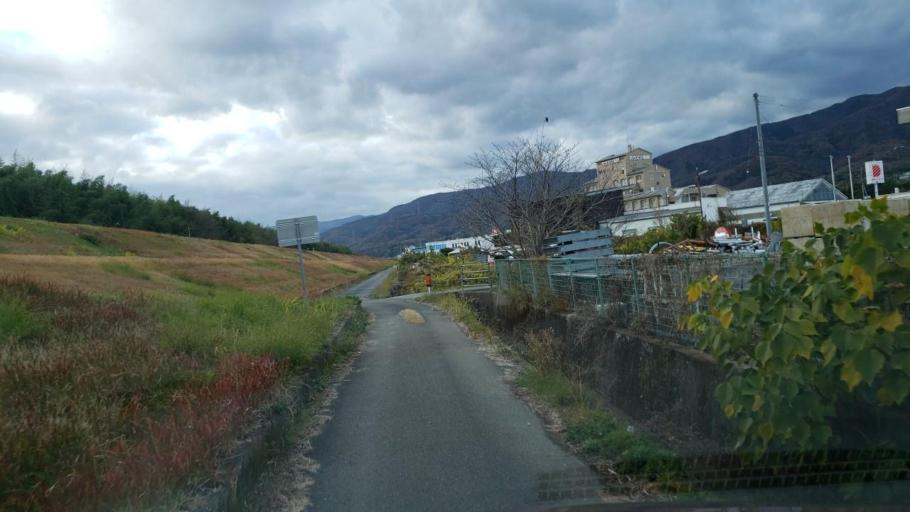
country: JP
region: Tokushima
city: Wakimachi
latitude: 34.0627
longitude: 134.1582
